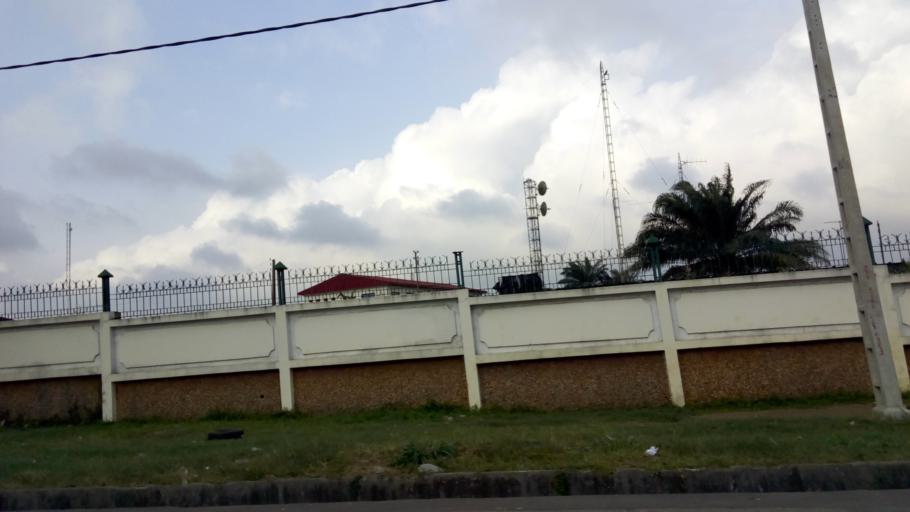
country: CI
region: Lagunes
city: Abidjan
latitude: 5.3369
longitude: -4.0255
